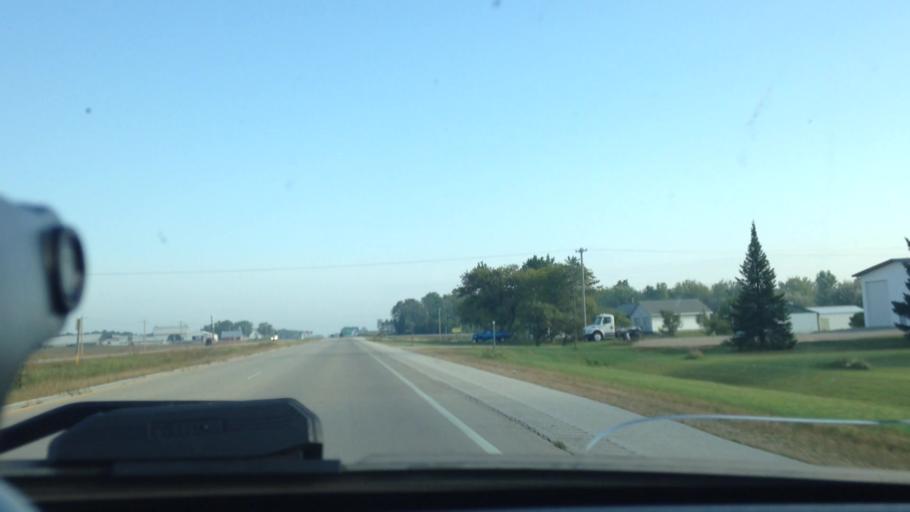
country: US
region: Wisconsin
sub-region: Oconto County
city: Oconto Falls
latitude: 45.0328
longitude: -88.0445
